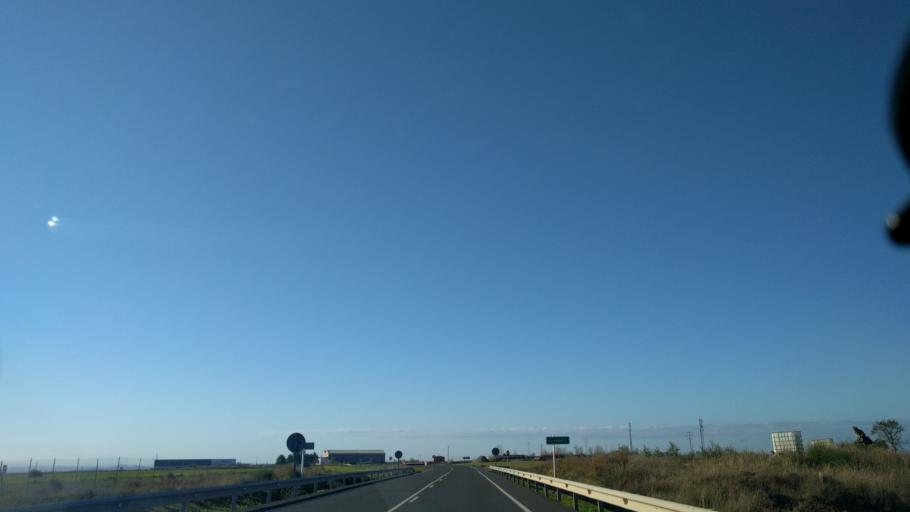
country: ES
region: Catalonia
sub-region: Provincia de Lleida
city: Termens
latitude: 41.7061
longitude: 0.7499
